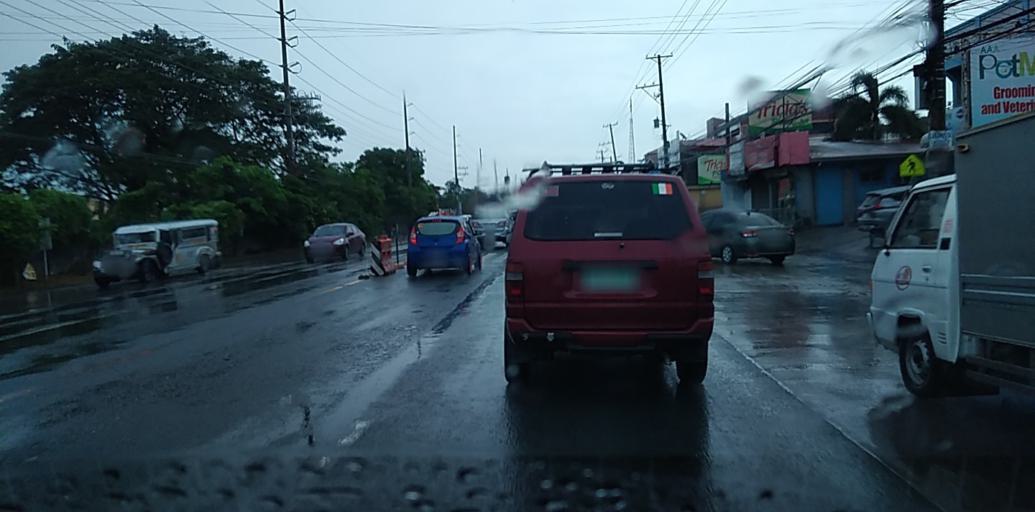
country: PH
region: Central Luzon
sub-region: Province of Pampanga
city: Bulaon
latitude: 15.0728
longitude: 120.6449
